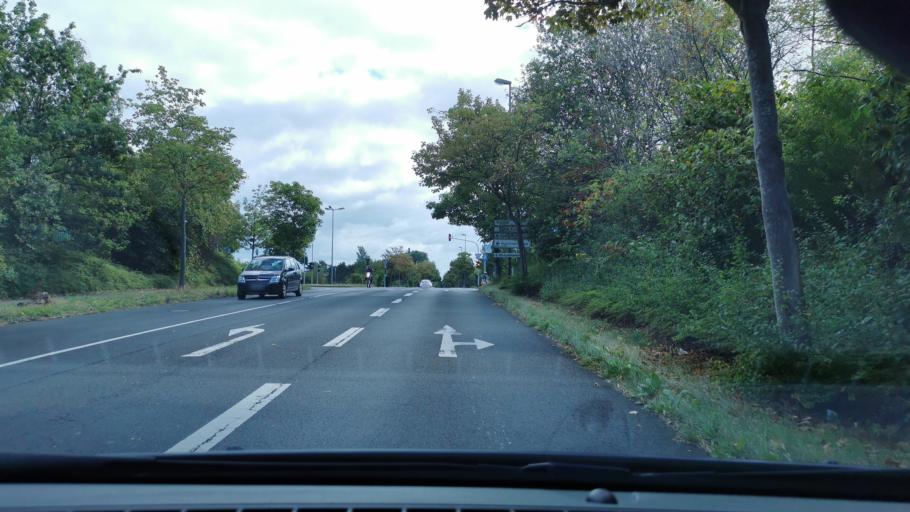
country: DE
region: North Rhine-Westphalia
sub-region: Regierungsbezirk Koln
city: Poll
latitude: 50.8699
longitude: 7.0039
